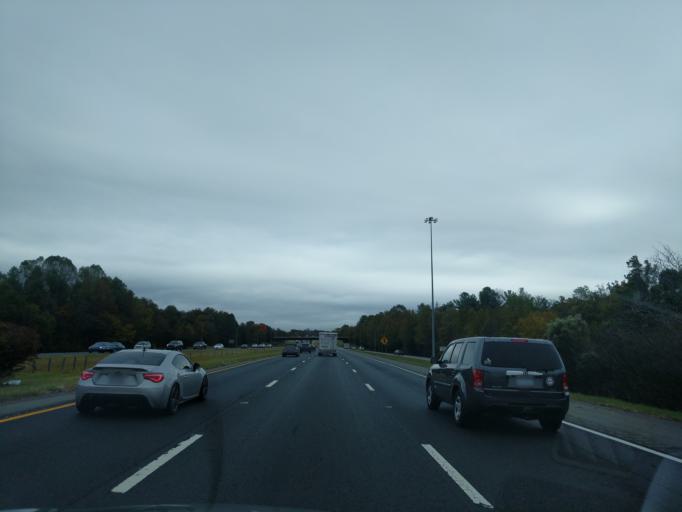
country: US
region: North Carolina
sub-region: Davidson County
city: Thomasville
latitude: 35.8603
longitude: -80.0736
